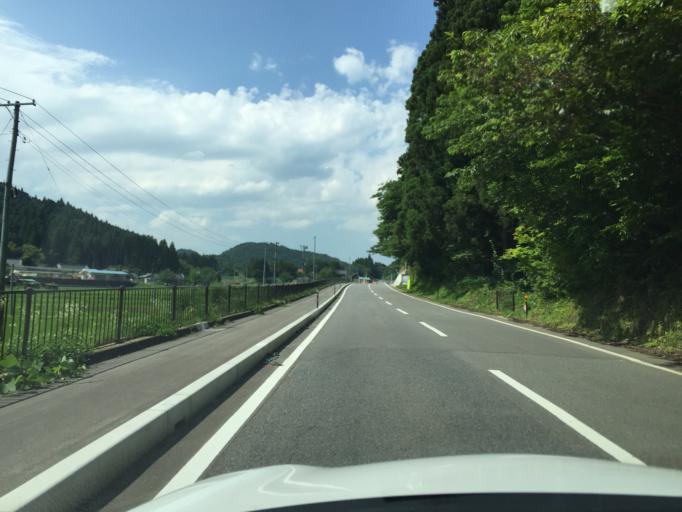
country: JP
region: Ibaraki
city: Kitaibaraki
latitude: 36.9593
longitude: 140.7039
